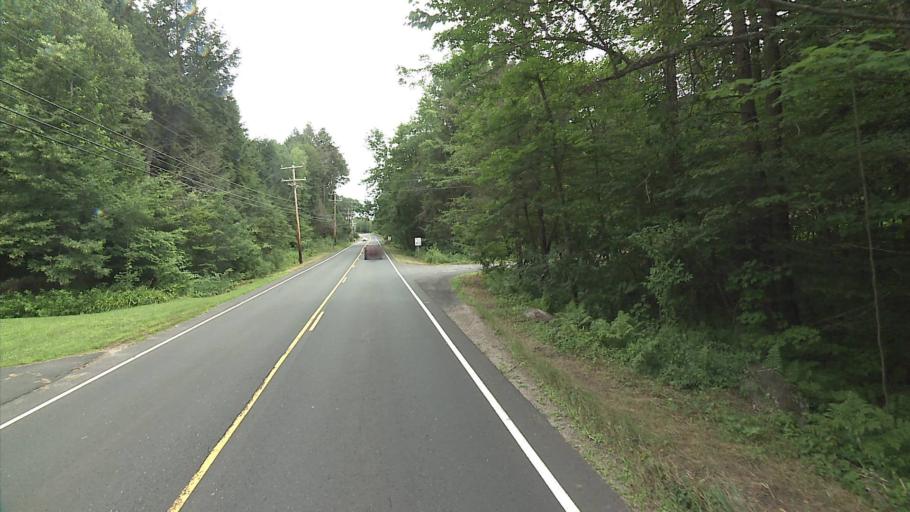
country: US
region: Connecticut
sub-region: Litchfield County
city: Winsted
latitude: 41.9909
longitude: -73.0466
